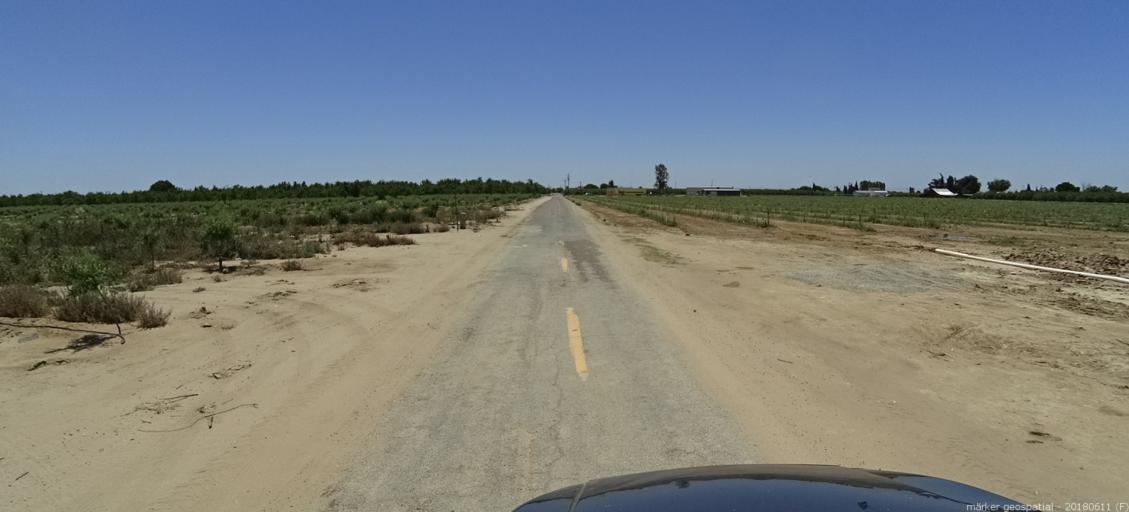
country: US
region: California
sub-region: Madera County
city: Fairmead
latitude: 37.0147
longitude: -120.1842
